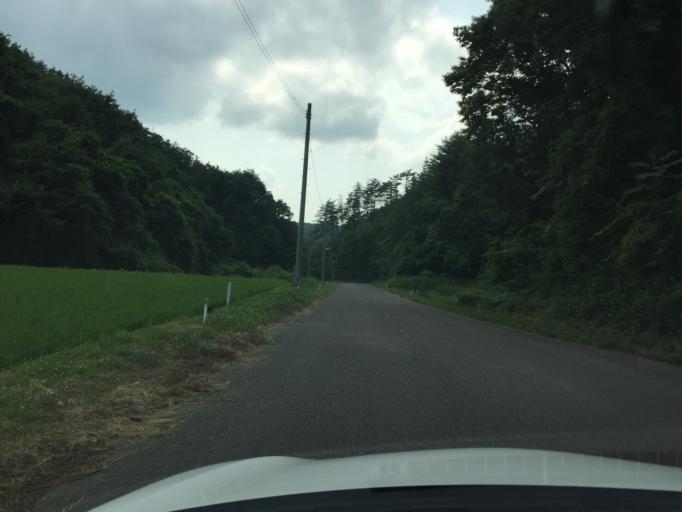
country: JP
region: Fukushima
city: Miharu
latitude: 37.3786
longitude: 140.4934
